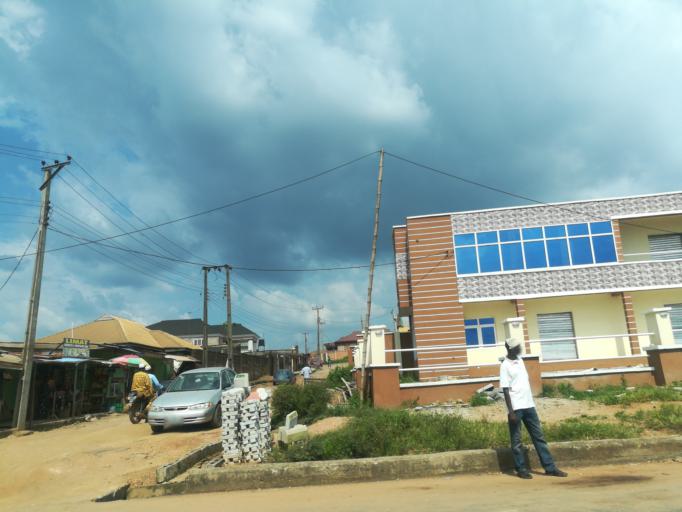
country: NG
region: Oyo
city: Ibadan
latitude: 7.4242
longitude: 3.8426
